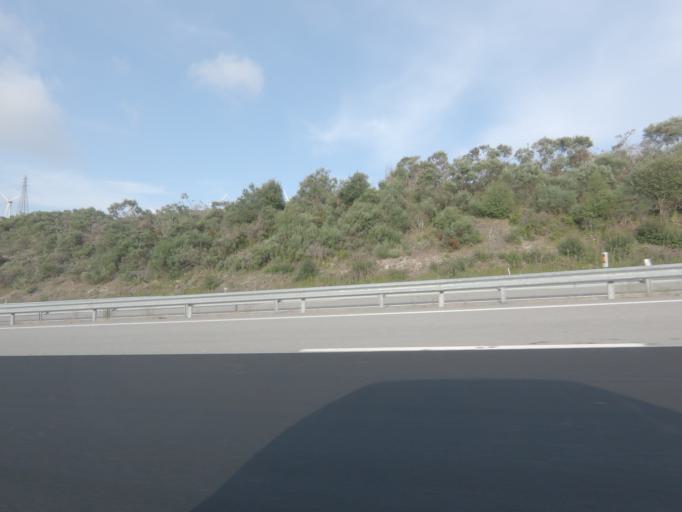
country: PT
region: Vila Real
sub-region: Vila Pouca de Aguiar
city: Vila Pouca de Aguiar
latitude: 41.4567
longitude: -7.6439
